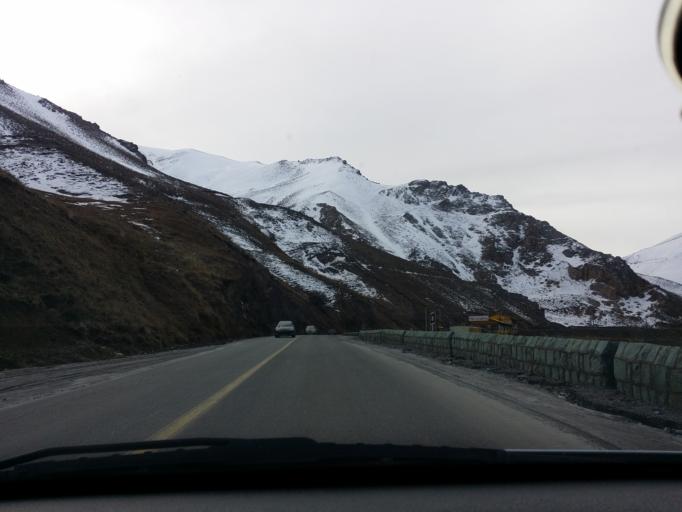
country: IR
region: Tehran
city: Tajrish
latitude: 36.1818
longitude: 51.3185
